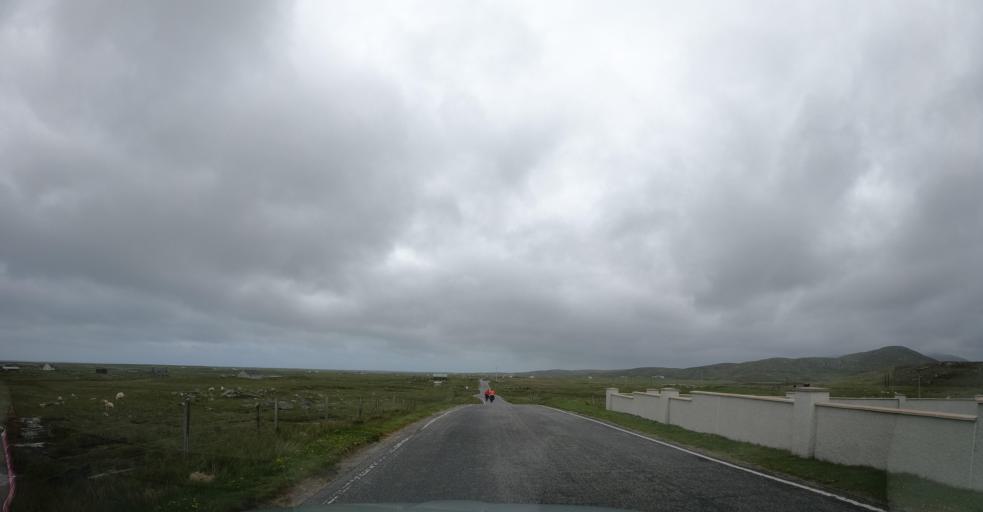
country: GB
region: Scotland
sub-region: Eilean Siar
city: Isle of South Uist
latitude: 57.2006
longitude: -7.3918
